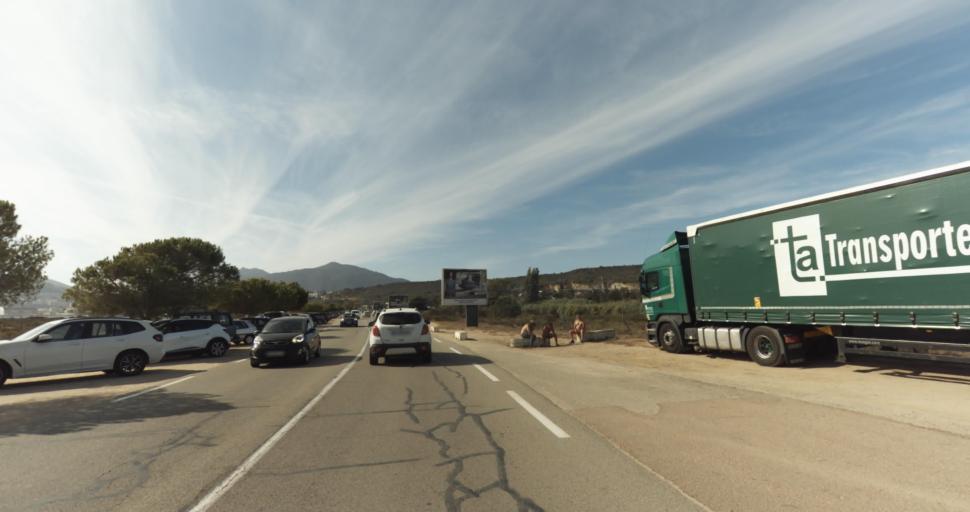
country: FR
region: Corsica
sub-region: Departement de la Corse-du-Sud
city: Ajaccio
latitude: 41.9244
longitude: 8.7831
